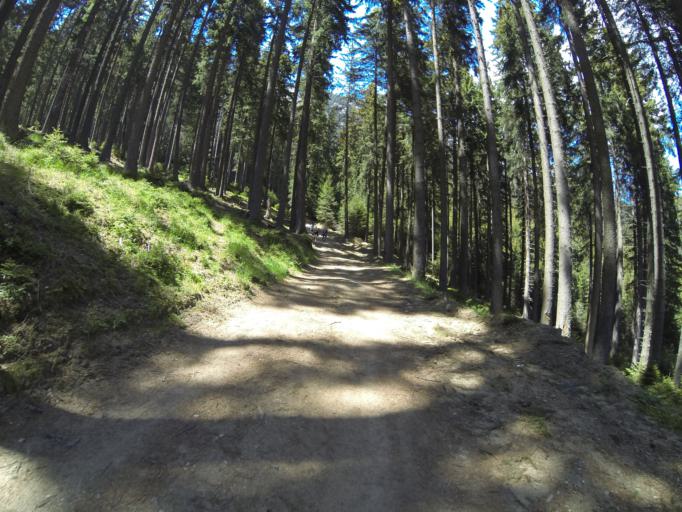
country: RO
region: Brasov
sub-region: Comuna Zarnesti
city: Zarnesti
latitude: 45.5474
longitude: 25.2507
